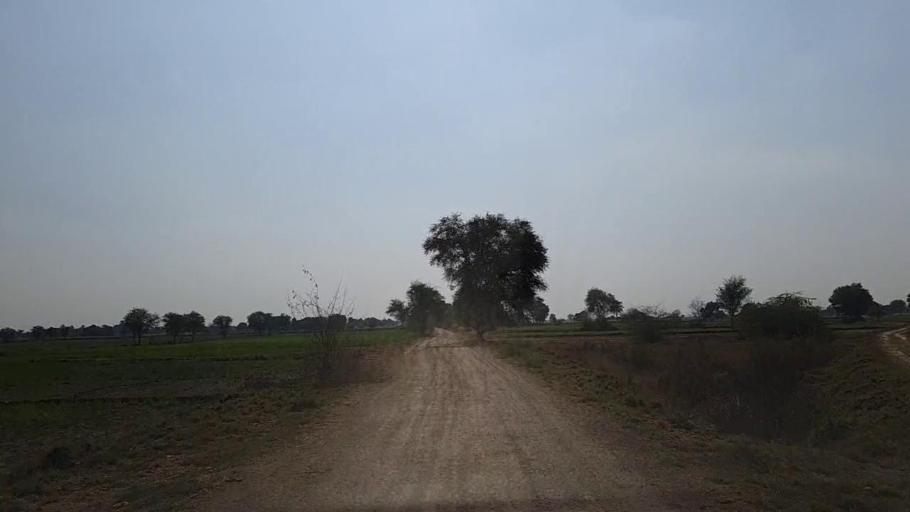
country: PK
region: Sindh
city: Nawabshah
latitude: 26.2562
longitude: 68.4899
